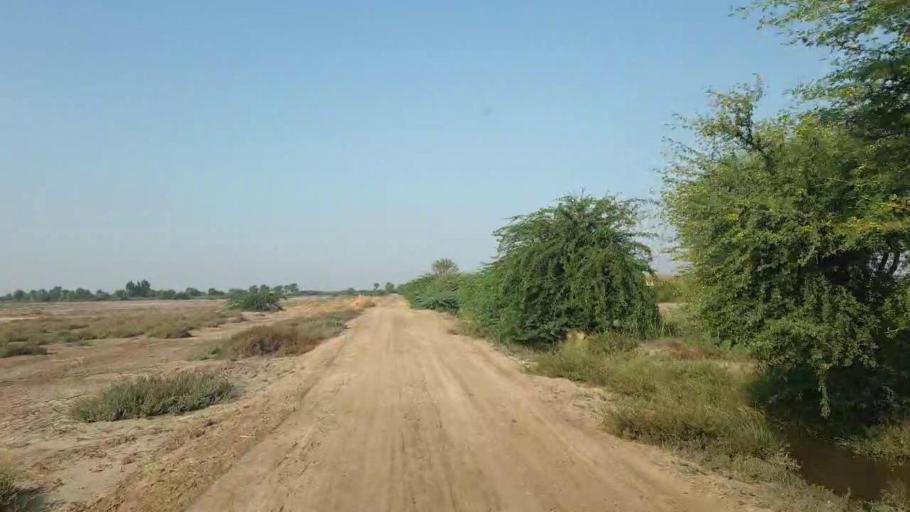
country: PK
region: Sindh
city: Badin
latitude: 24.4539
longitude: 68.7298
